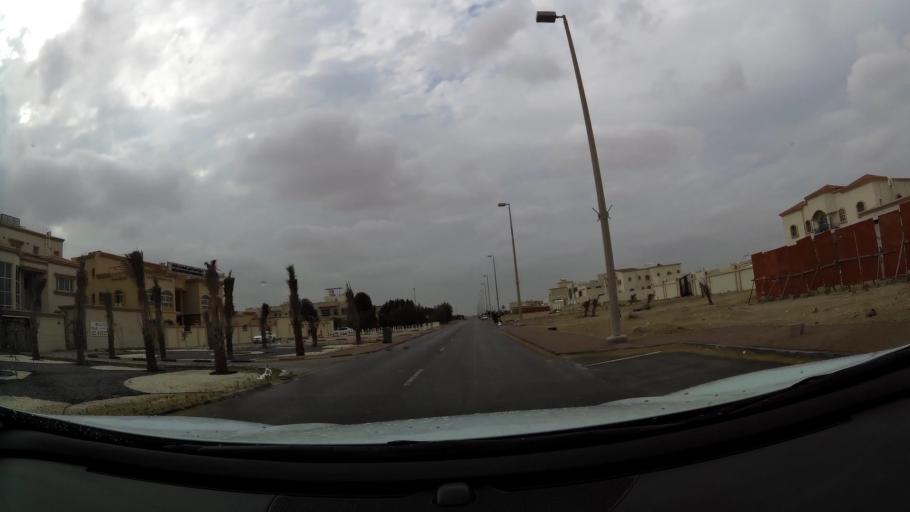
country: AE
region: Abu Dhabi
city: Abu Dhabi
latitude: 24.3602
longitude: 54.6227
